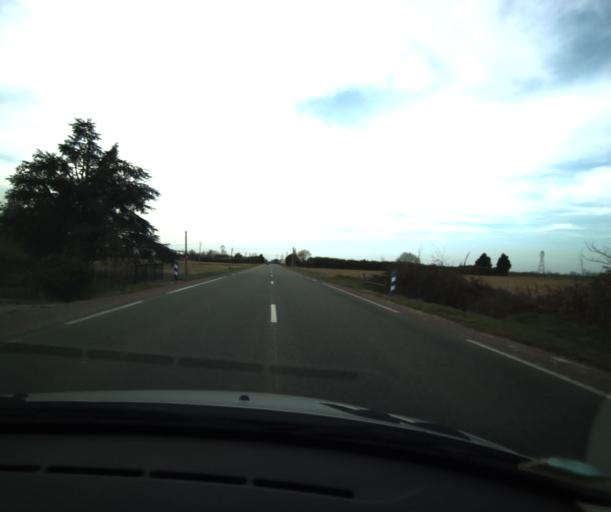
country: FR
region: Midi-Pyrenees
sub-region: Departement du Tarn-et-Garonne
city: Montech
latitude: 43.9720
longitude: 1.2040
